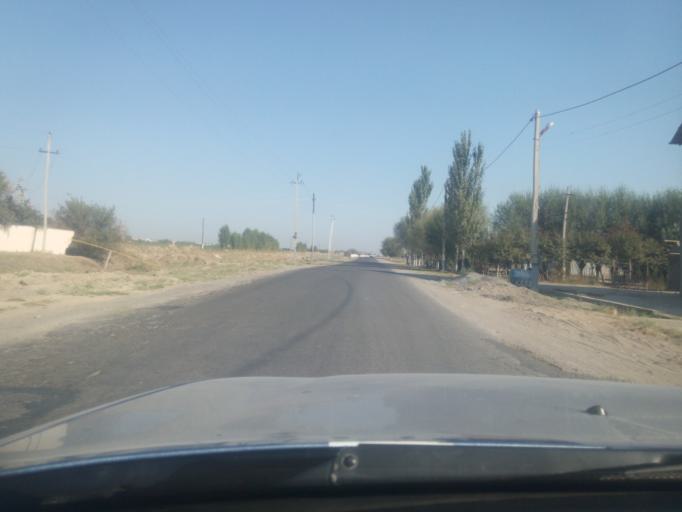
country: UZ
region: Sirdaryo
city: Guliston
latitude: 40.4966
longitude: 68.7997
